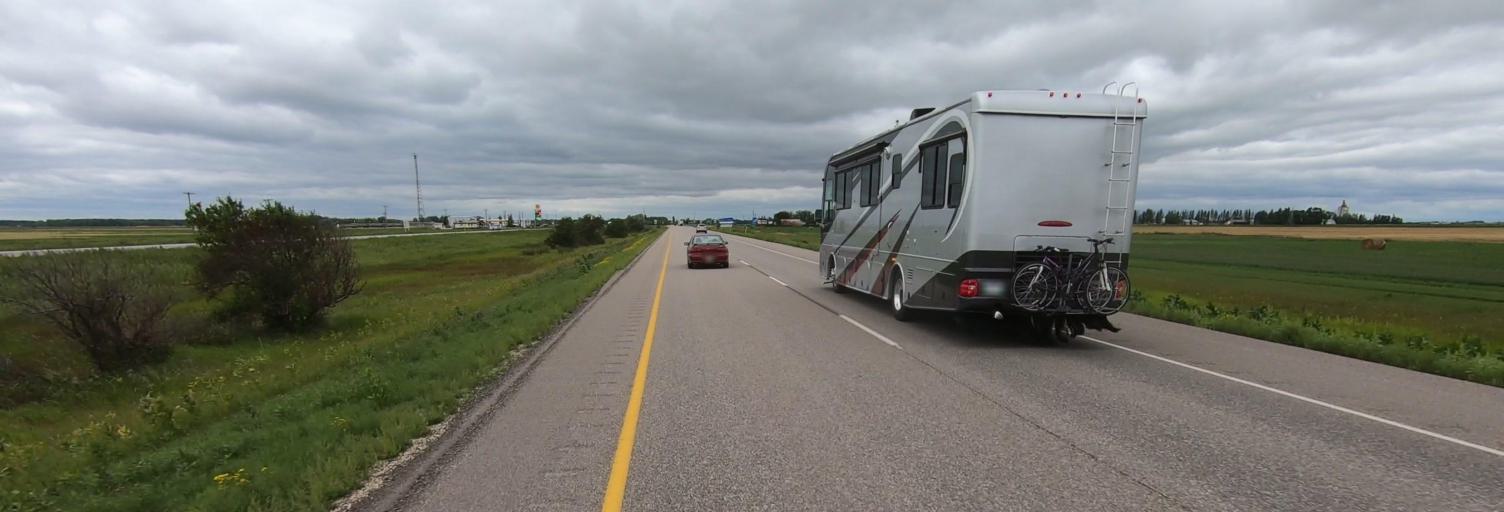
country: CA
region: Manitoba
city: Portage la Prairie
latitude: 49.9753
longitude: -98.2034
